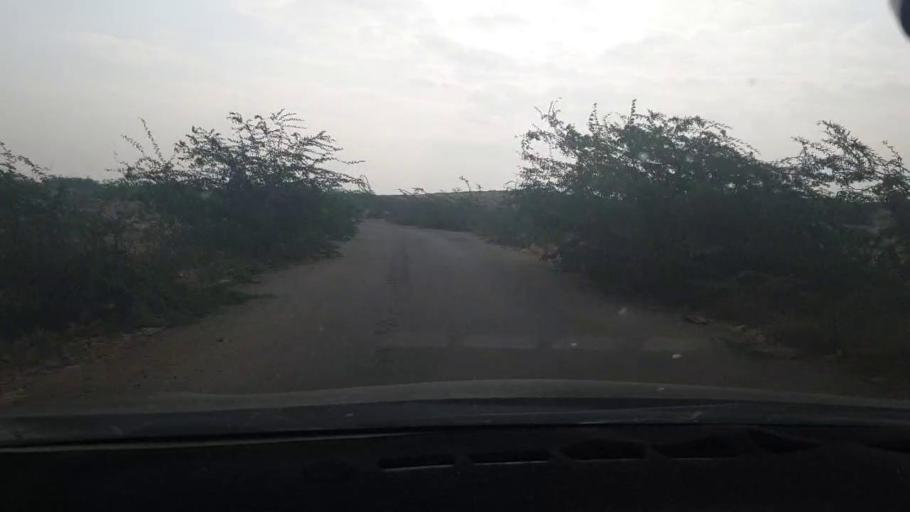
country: PK
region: Sindh
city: Malir Cantonment
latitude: 24.9526
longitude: 67.4254
